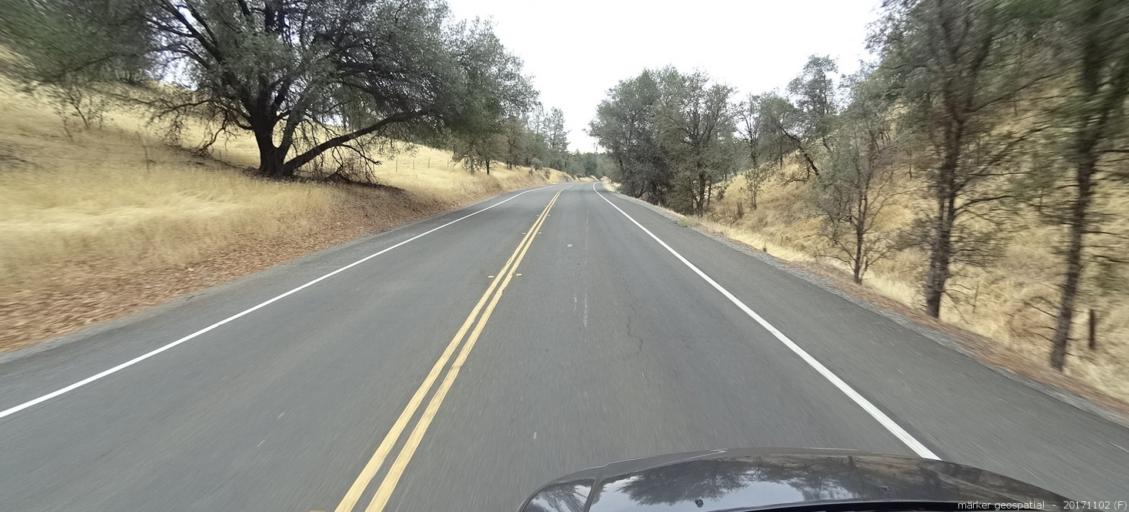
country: US
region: California
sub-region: Shasta County
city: Bella Vista
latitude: 40.6992
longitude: -122.2455
